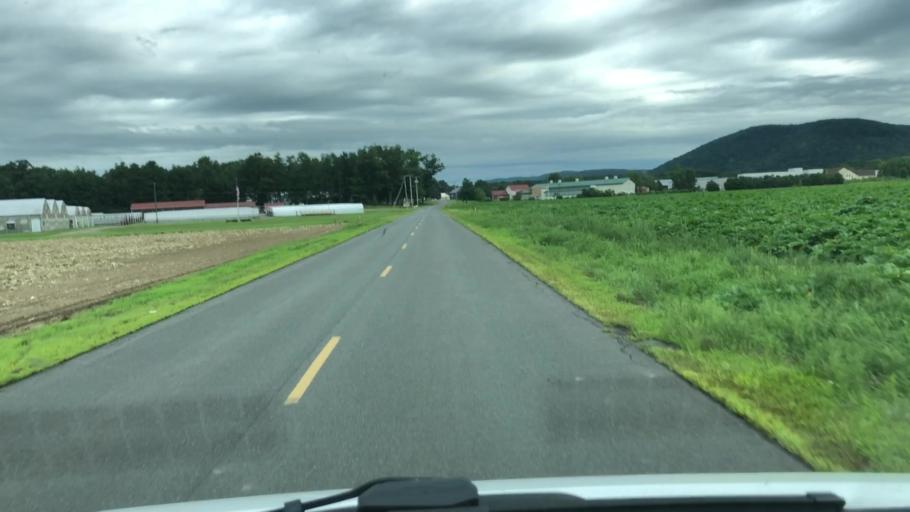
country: US
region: Massachusetts
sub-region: Franklin County
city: South Deerfield
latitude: 42.4576
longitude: -72.6092
